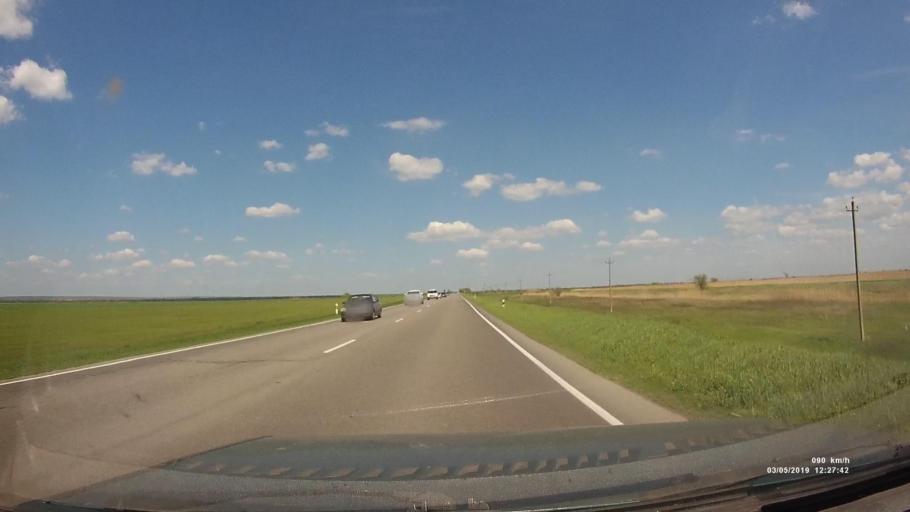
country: RU
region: Rostov
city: Semikarakorsk
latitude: 47.4629
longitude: 40.7232
